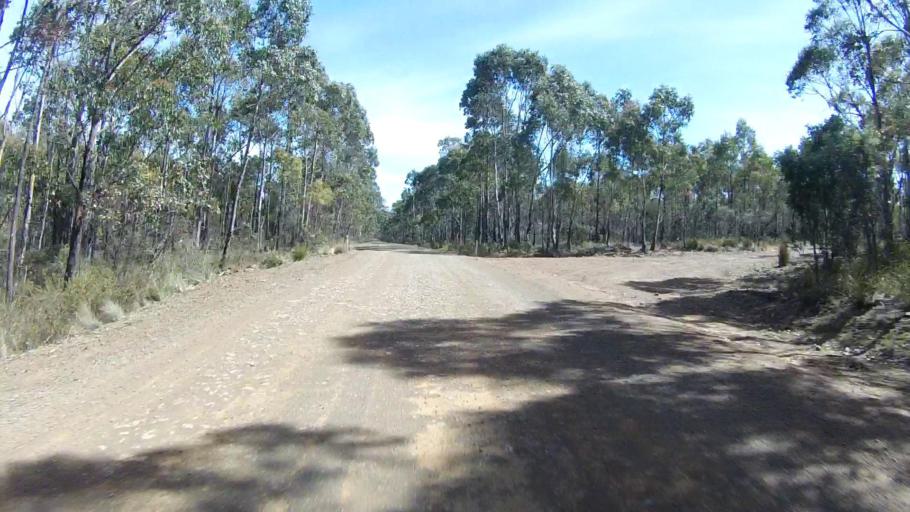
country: AU
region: Tasmania
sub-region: Sorell
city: Sorell
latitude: -42.6783
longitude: 147.7308
